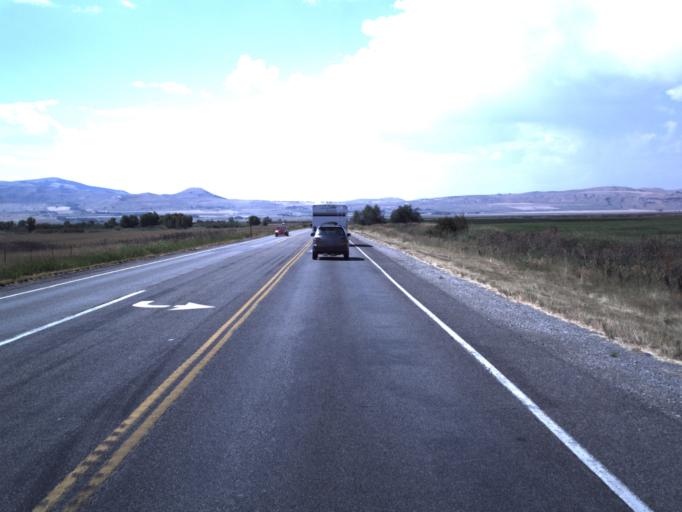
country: US
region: Utah
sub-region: Cache County
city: Benson
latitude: 41.7416
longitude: -111.9114
